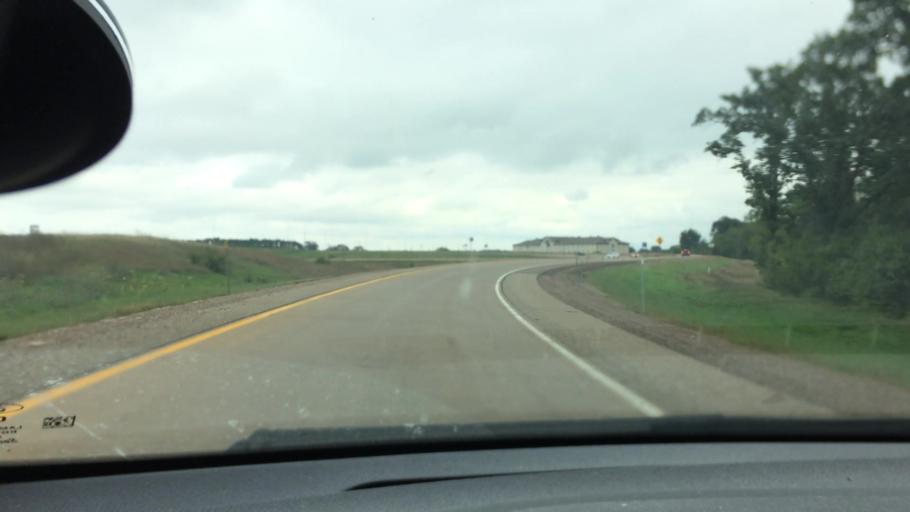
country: US
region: Wisconsin
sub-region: Chippewa County
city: Lake Hallie
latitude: 44.8786
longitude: -91.4166
